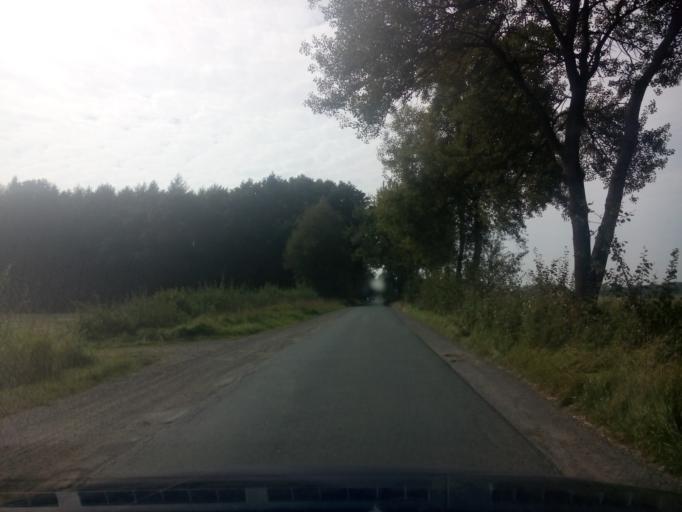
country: DE
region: Lower Saxony
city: Osterholz-Scharmbeck
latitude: 53.2618
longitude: 8.7694
